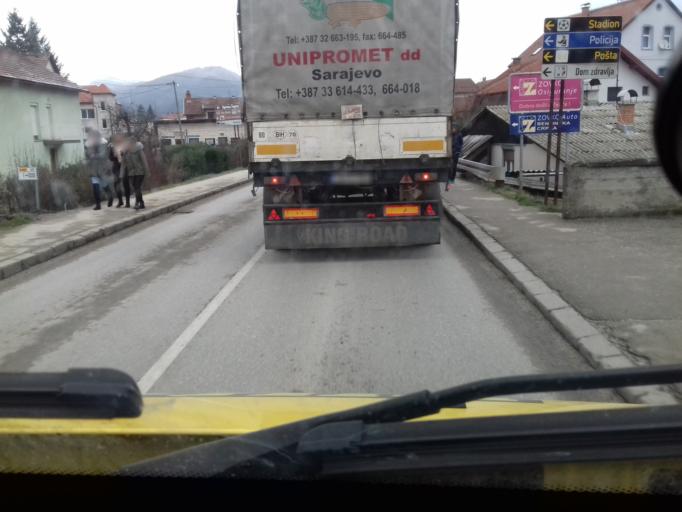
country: BA
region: Federation of Bosnia and Herzegovina
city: Zepce
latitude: 44.4235
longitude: 18.0408
